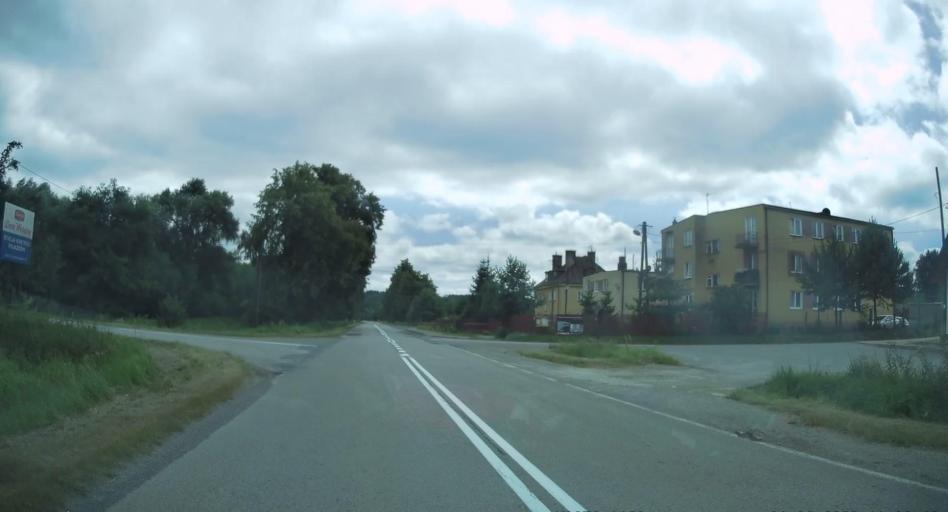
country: PL
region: Swietokrzyskie
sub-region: Powiat sandomierski
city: Klimontow
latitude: 50.6638
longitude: 21.4215
